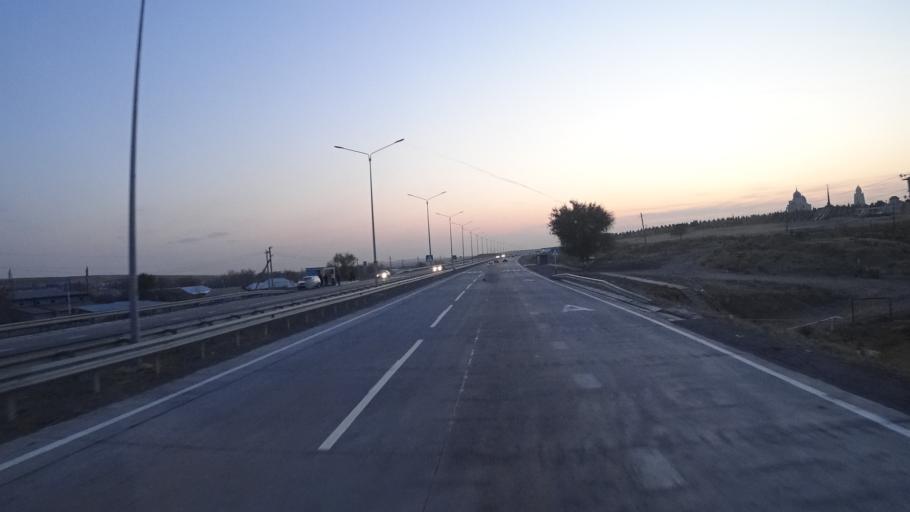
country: KZ
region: Ongtustik Qazaqstan
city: Qazyqurt
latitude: 41.8782
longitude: 69.4336
